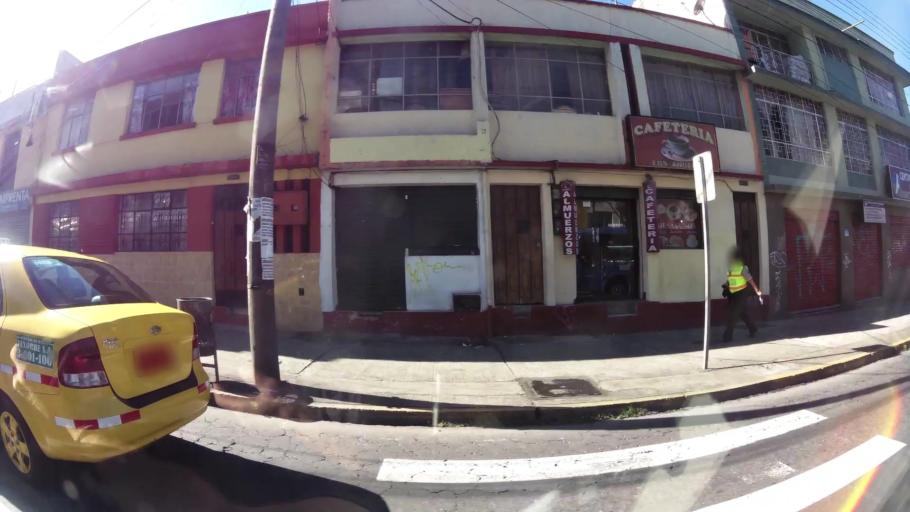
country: EC
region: Pichincha
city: Quito
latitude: -0.2368
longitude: -78.5277
